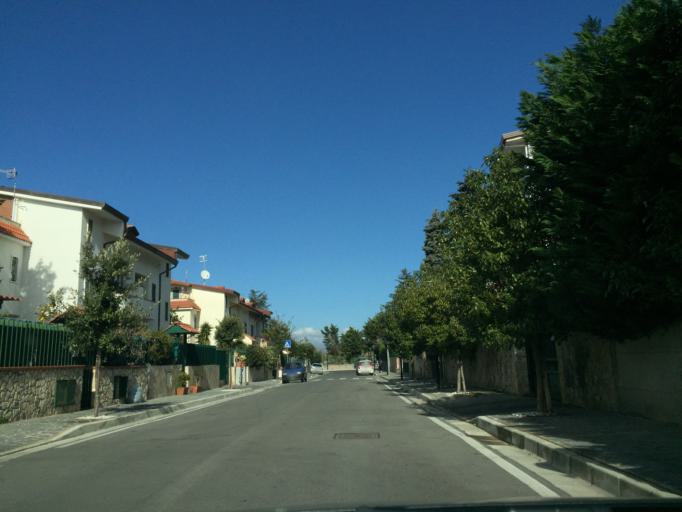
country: IT
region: Campania
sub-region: Provincia di Napoli
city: Pollena Trocchia
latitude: 40.8494
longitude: 14.3821
